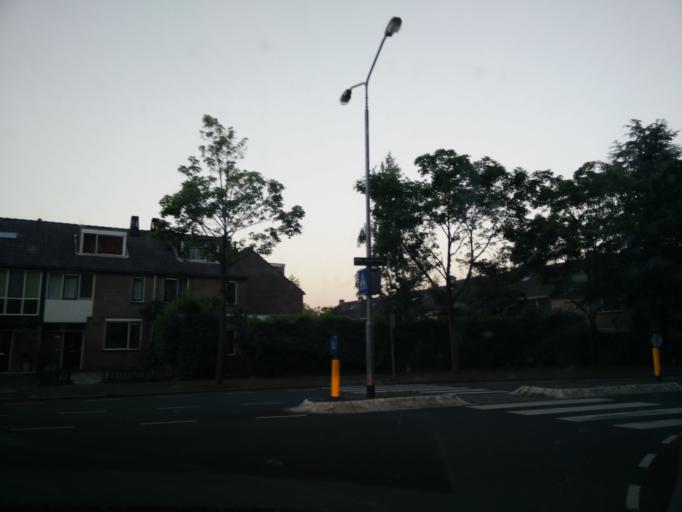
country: NL
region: South Holland
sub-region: Gemeente Dordrecht
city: Dordrecht
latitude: 51.7814
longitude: 4.6826
